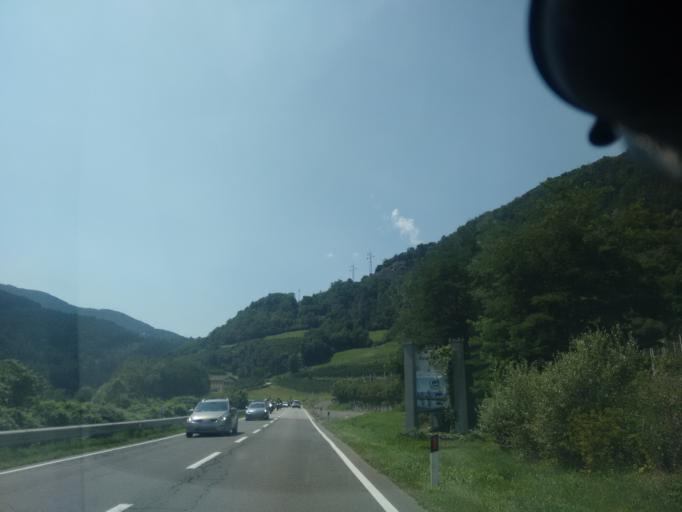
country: IT
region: Trentino-Alto Adige
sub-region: Bolzano
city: Velturno
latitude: 46.6647
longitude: 11.6099
